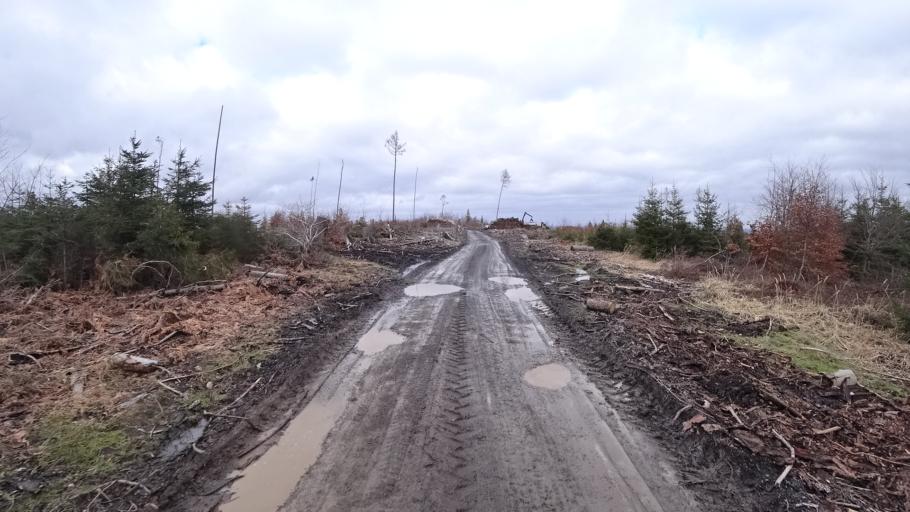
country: DE
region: Rheinland-Pfalz
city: Dernbach
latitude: 50.4308
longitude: 7.7661
